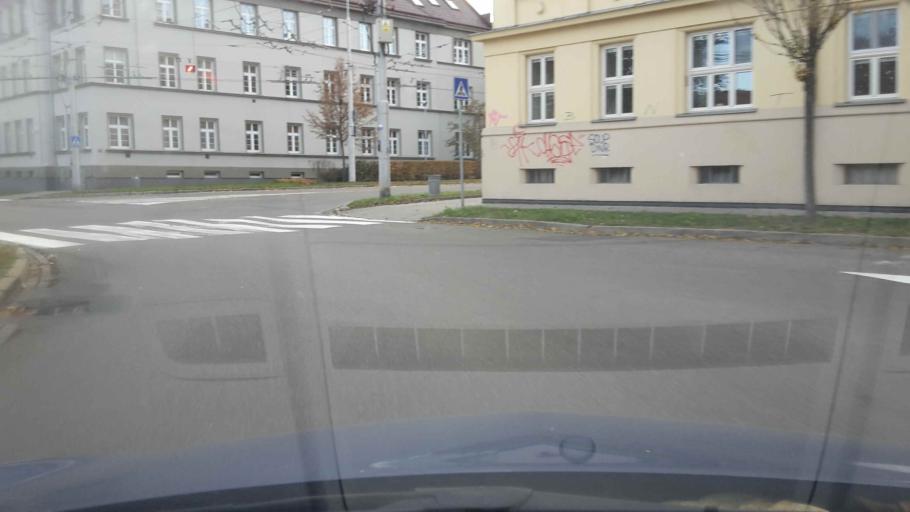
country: CZ
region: South Moravian
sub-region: Mesto Brno
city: Brno
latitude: 49.2232
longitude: 16.5901
